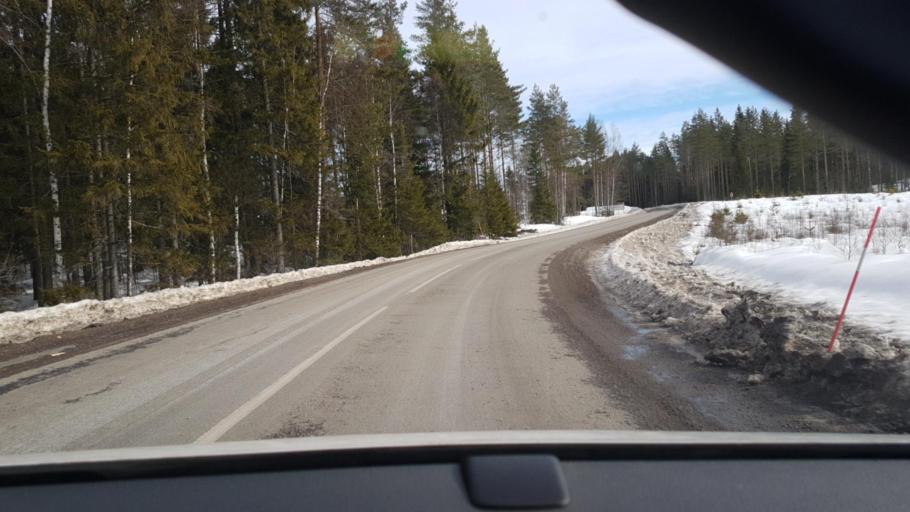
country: SE
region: Vaermland
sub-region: Eda Kommun
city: Amotfors
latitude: 59.6008
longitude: 12.3084
